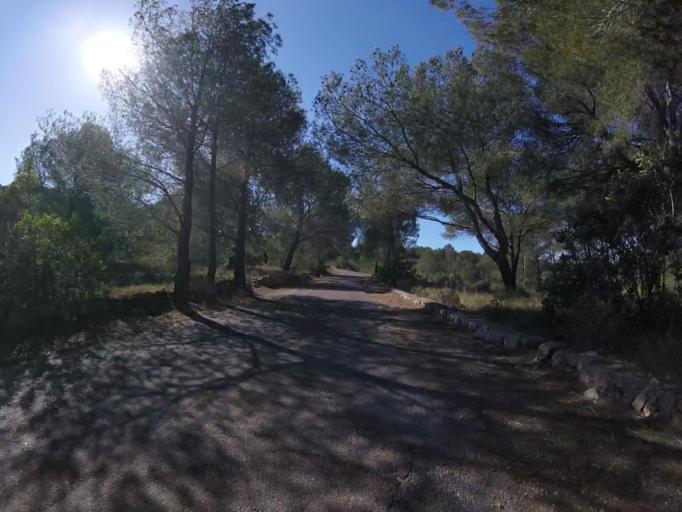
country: ES
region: Valencia
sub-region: Provincia de Castello
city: Orpesa/Oropesa del Mar
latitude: 40.0849
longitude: 0.1240
